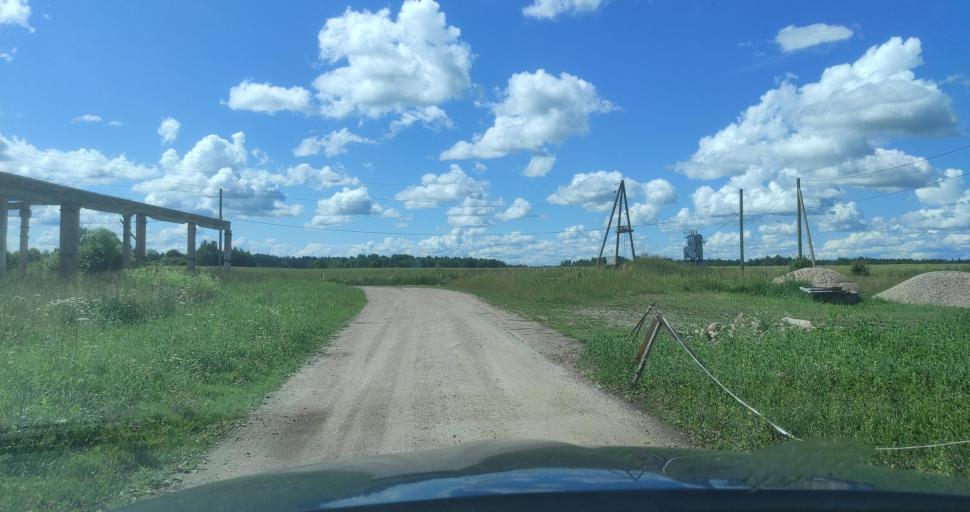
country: LV
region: Kuldigas Rajons
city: Kuldiga
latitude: 57.0026
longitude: 22.1292
